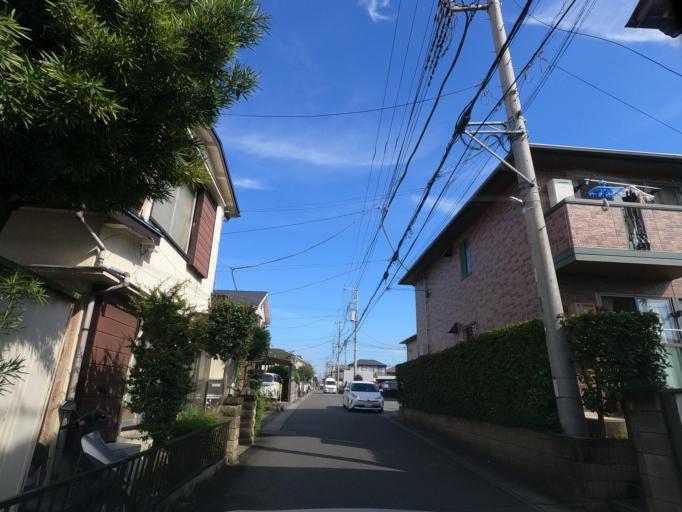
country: JP
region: Saitama
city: Yono
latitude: 35.8797
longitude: 139.6106
